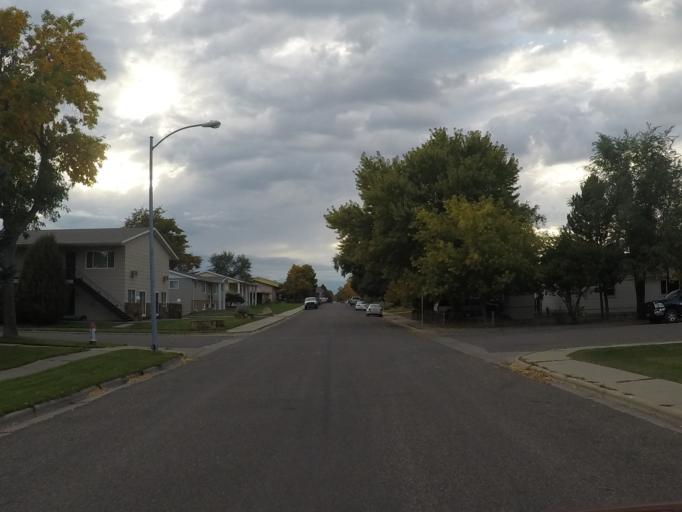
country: US
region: Montana
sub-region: Yellowstone County
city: Billings
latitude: 45.7880
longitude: -108.5328
